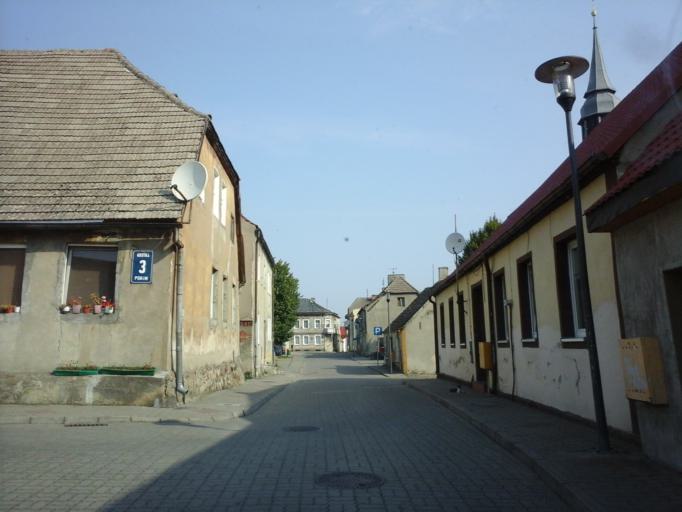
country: PL
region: West Pomeranian Voivodeship
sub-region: Powiat choszczenski
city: Pelczyce
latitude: 53.0411
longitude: 15.2995
